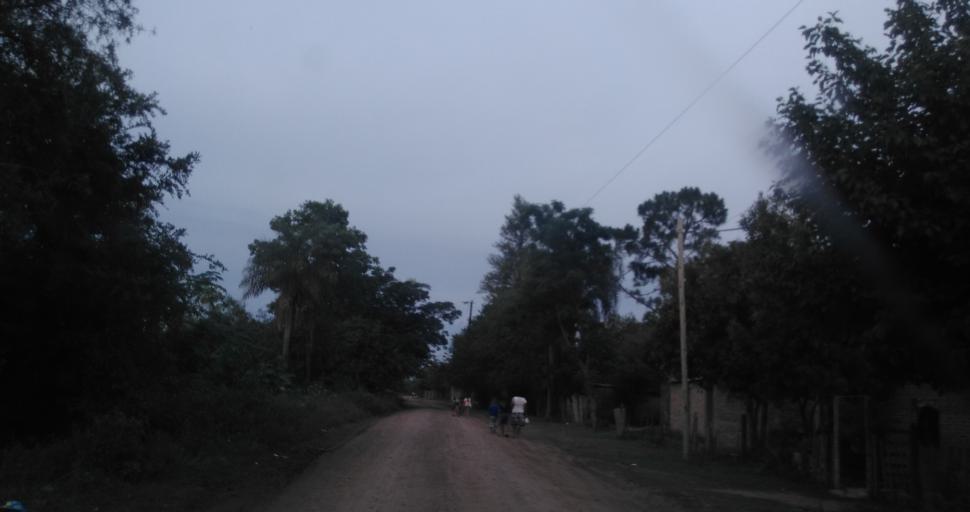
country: AR
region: Chaco
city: Fontana
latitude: -27.4081
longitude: -59.0264
